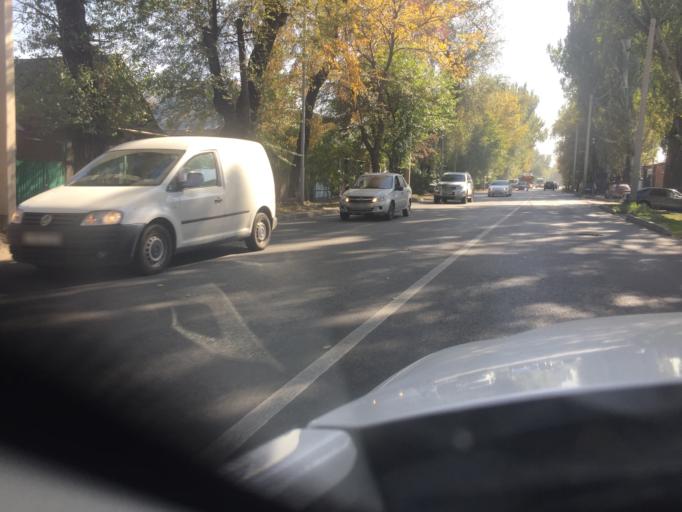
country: KZ
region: Almaty Qalasy
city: Almaty
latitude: 43.2635
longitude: 76.9107
